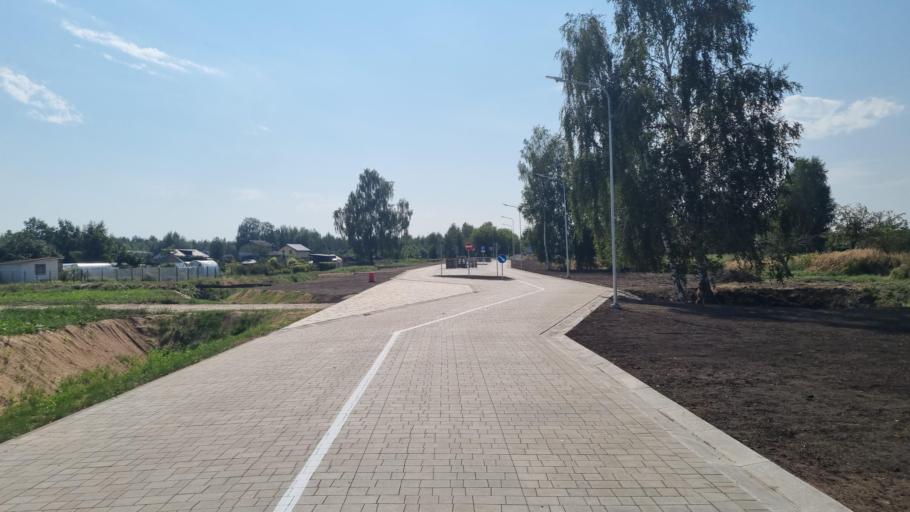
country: LV
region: Marupe
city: Marupe
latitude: 56.8807
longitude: 24.0626
